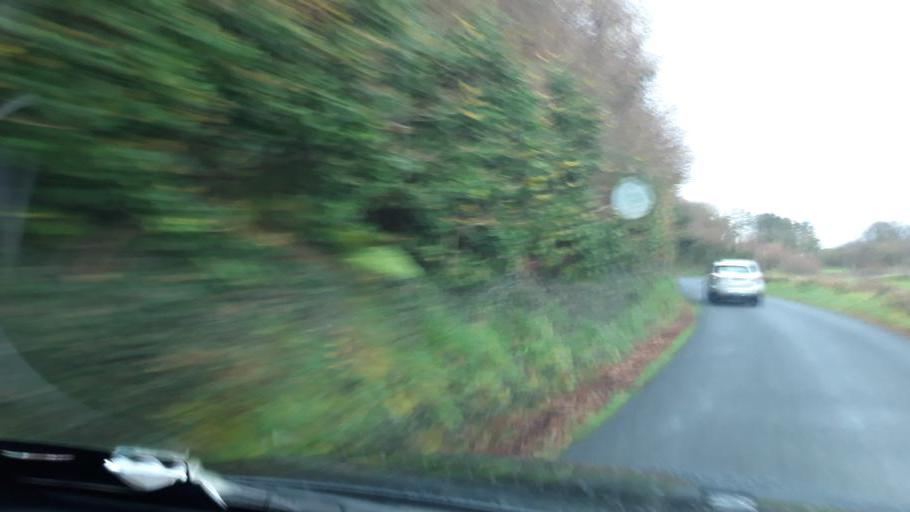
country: IE
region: Ulster
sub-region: County Donegal
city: Buncrana
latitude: 55.2332
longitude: -7.6175
